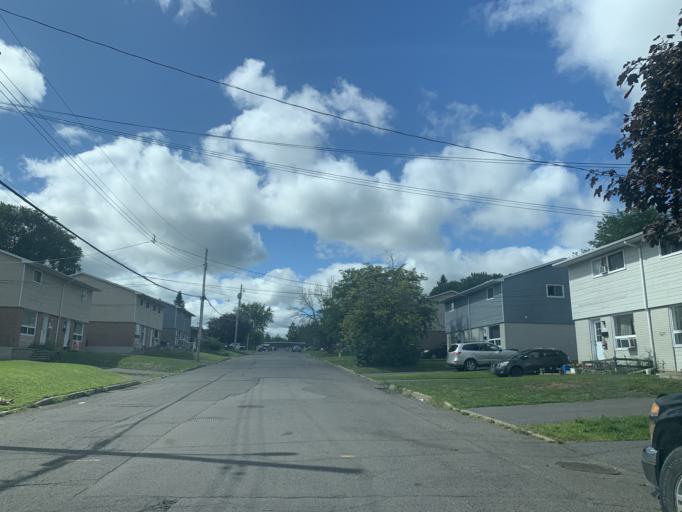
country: CA
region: Ontario
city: Hawkesbury
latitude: 45.6045
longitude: -74.5856
